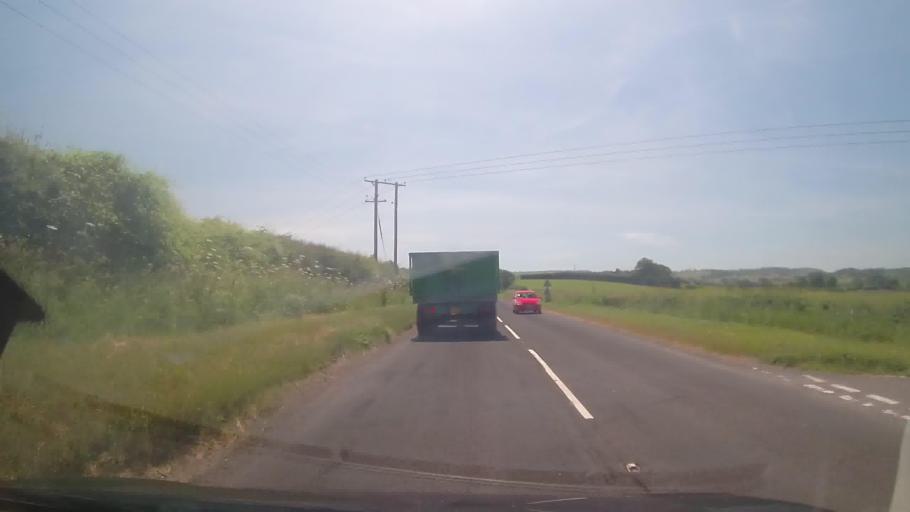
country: GB
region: England
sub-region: Herefordshire
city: Pencoyd
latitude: 51.9117
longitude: -2.7342
